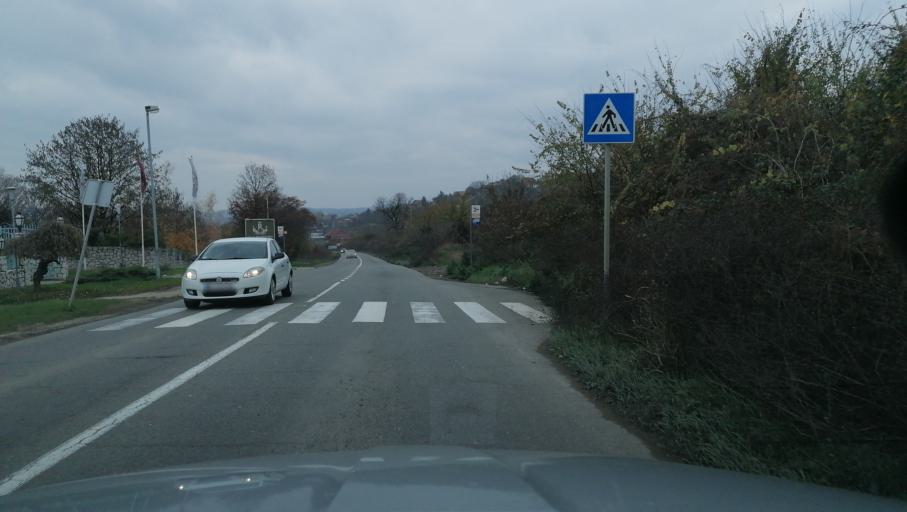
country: RS
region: Central Serbia
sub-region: Belgrade
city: Zvezdara
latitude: 44.7539
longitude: 20.5807
